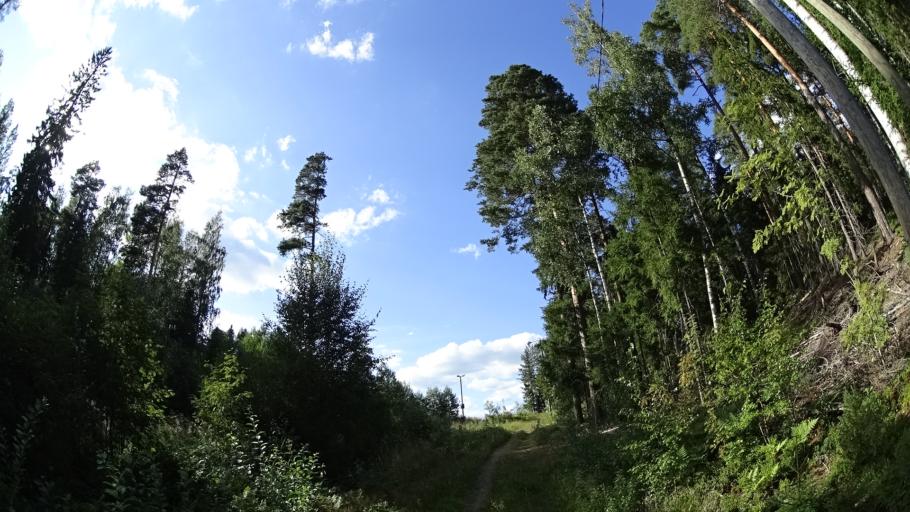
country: FI
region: Uusimaa
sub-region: Helsinki
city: Vihti
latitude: 60.3759
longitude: 24.3717
